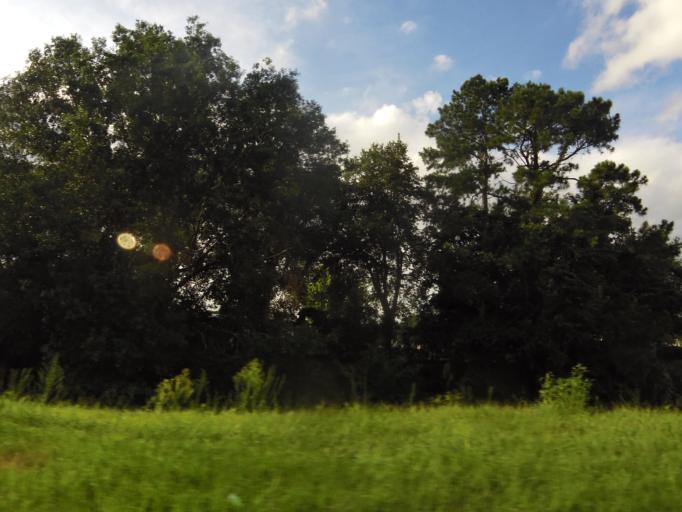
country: US
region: Florida
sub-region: Duval County
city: Jacksonville
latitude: 30.3214
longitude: -81.7408
